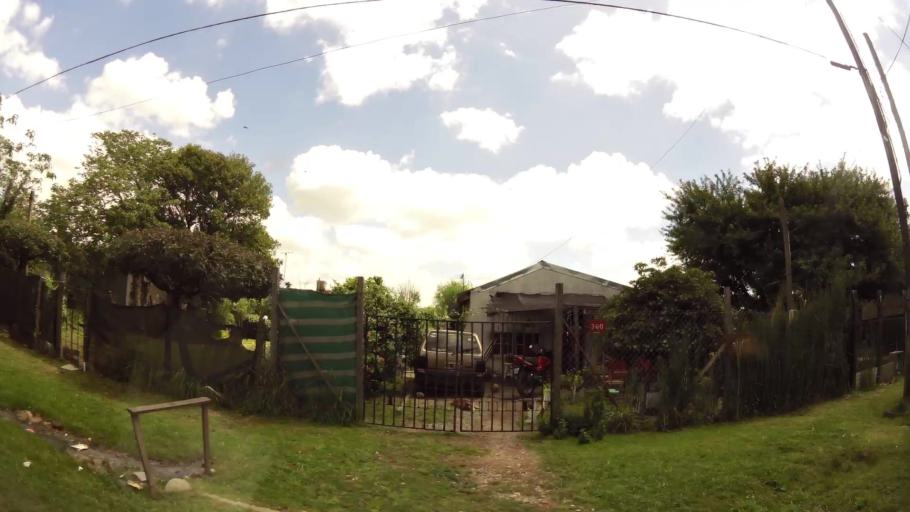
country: AR
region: Buenos Aires
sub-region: Partido de Quilmes
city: Quilmes
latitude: -34.8267
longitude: -58.2439
